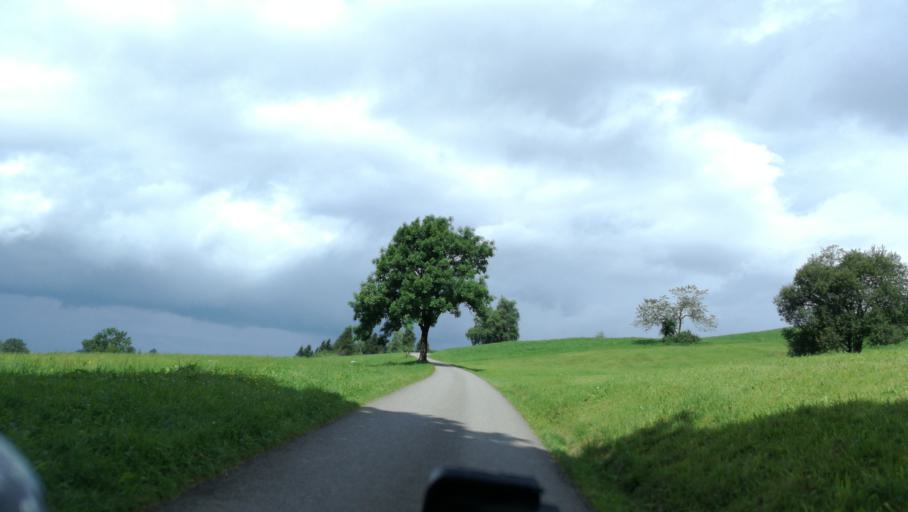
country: CH
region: Zug
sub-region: Zug
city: Walchwil
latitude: 47.1028
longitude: 8.5478
